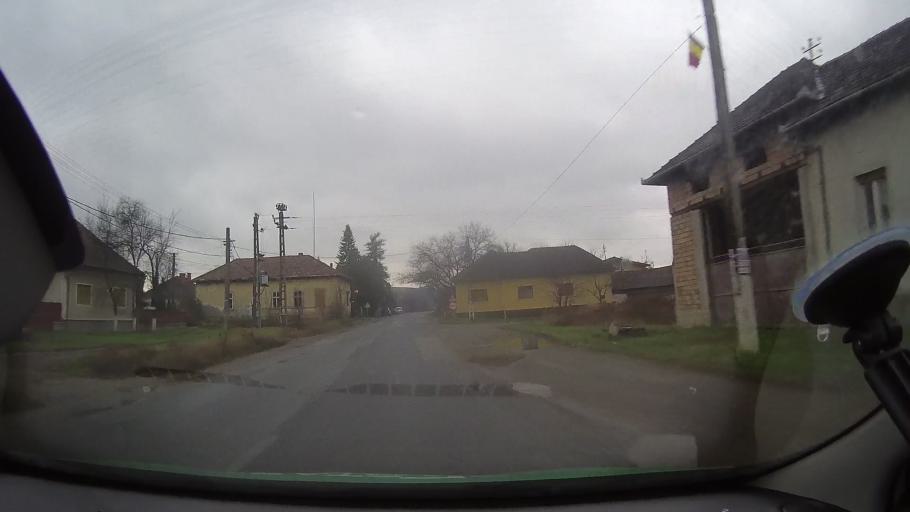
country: RO
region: Arad
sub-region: Comuna Halmagiu
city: Halmagiu
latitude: 46.2682
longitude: 22.5969
